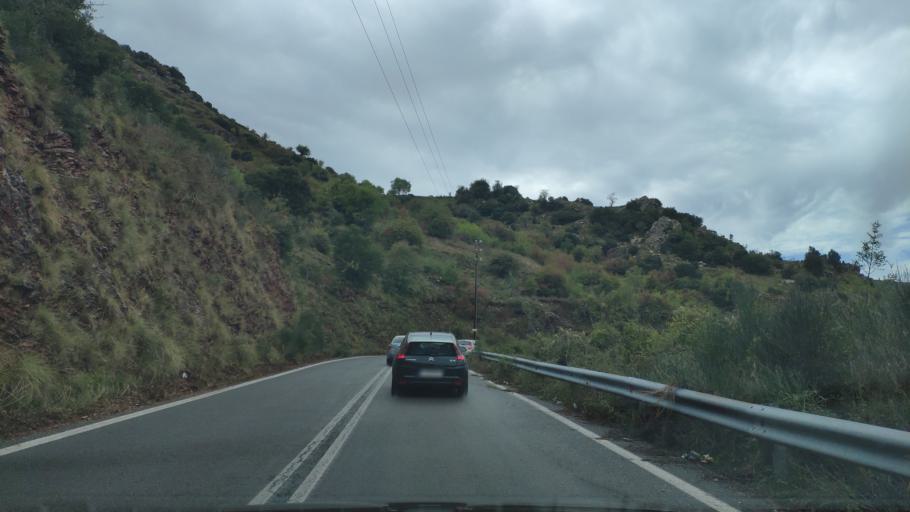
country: GR
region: Peloponnese
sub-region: Nomos Arkadias
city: Dimitsana
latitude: 37.6067
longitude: 22.0424
